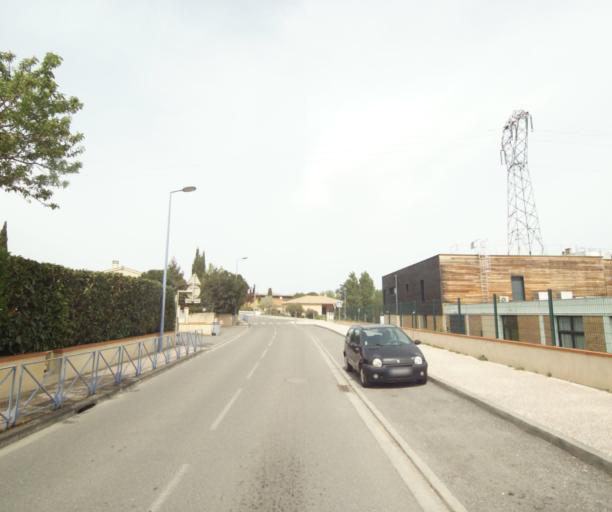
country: FR
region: Midi-Pyrenees
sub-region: Departement de la Haute-Garonne
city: Castanet-Tolosan
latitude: 43.5192
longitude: 1.4947
